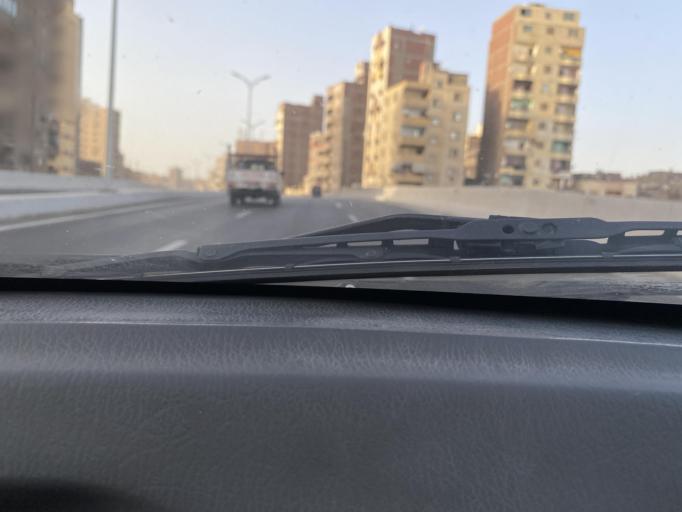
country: EG
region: Muhafazat al Qahirah
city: Cairo
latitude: 30.1187
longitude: 31.2972
